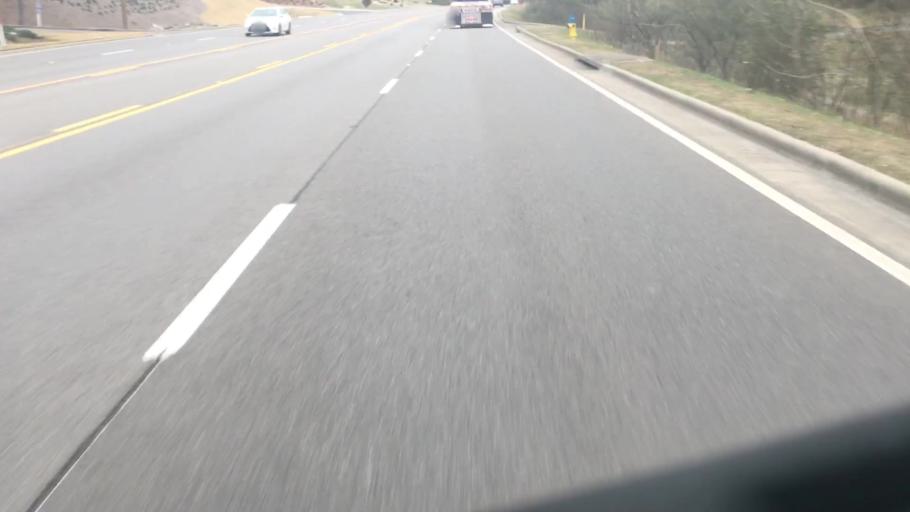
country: US
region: Alabama
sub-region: Jefferson County
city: Hoover
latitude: 33.3676
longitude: -86.8206
